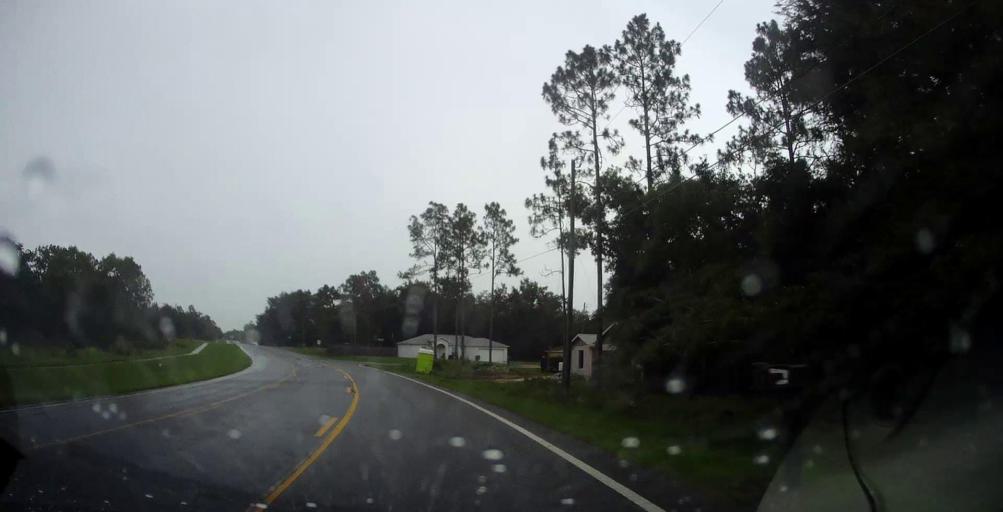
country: US
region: Florida
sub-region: Marion County
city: Silver Springs Shores
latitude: 29.1142
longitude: -82.0184
